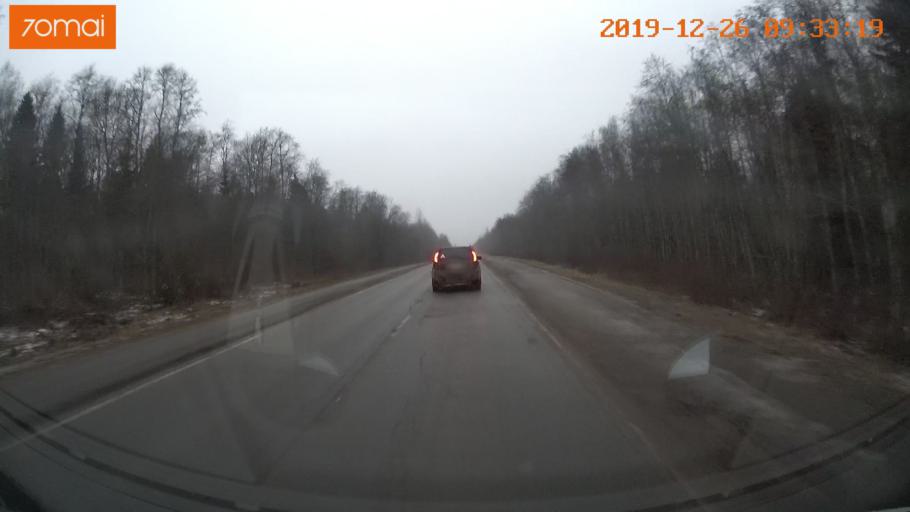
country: RU
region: Vologda
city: Vologda
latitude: 59.0885
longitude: 40.1023
